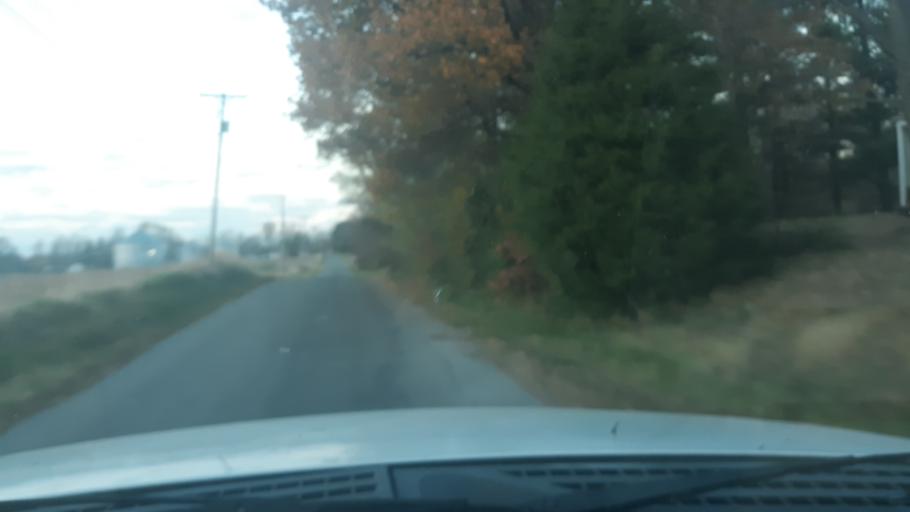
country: US
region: Illinois
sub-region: Saline County
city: Harrisburg
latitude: 37.8452
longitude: -88.6145
